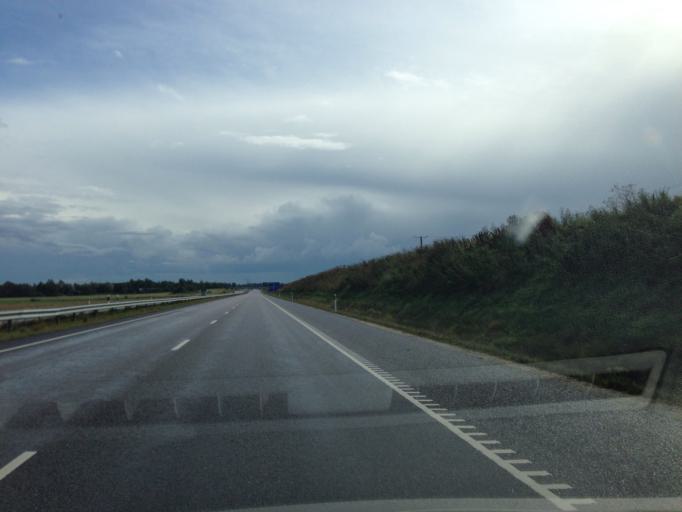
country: EE
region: Jaervamaa
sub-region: Paide linn
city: Paide
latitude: 58.9281
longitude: 25.6125
